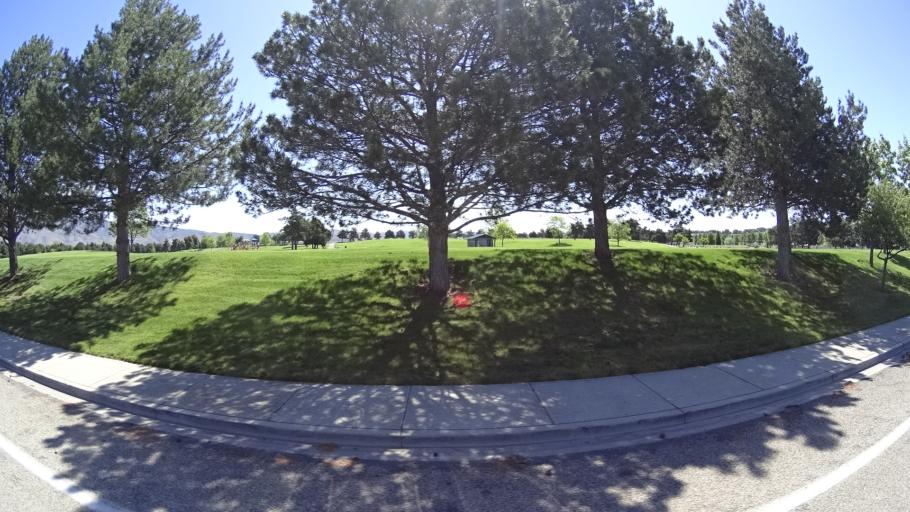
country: US
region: Idaho
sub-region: Ada County
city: Boise
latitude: 43.5484
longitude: -116.1536
